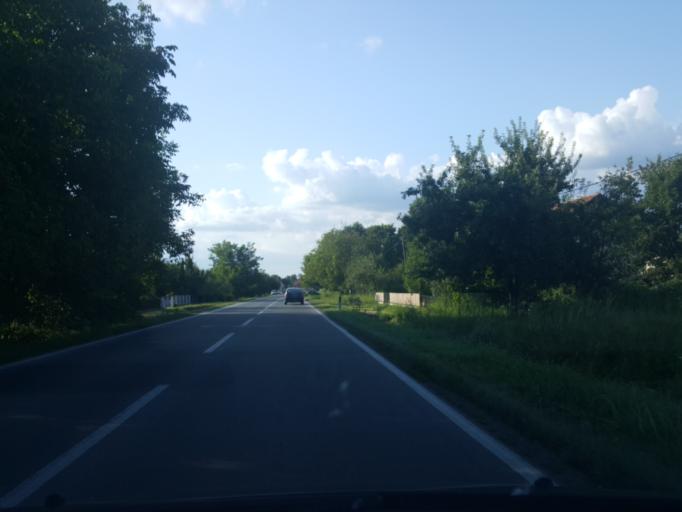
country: RS
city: Lipnicki Sor
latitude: 44.5987
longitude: 19.2555
